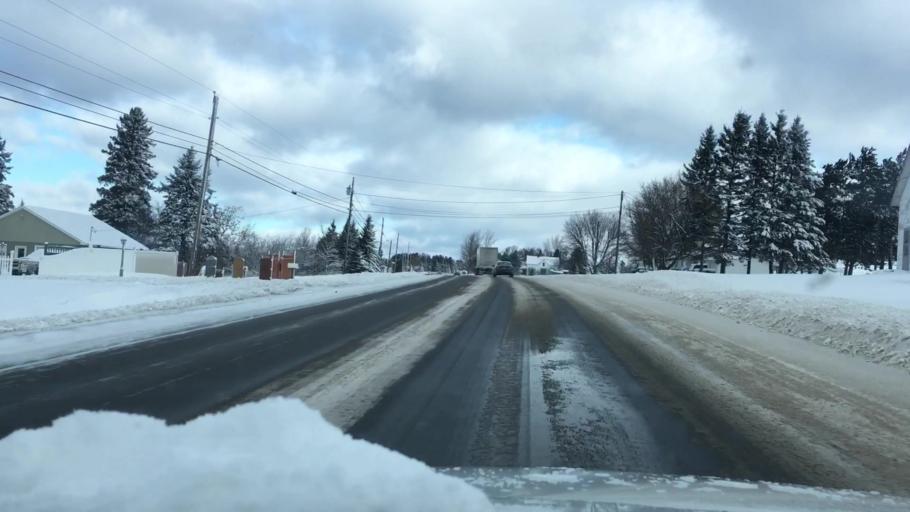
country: US
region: Maine
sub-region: Aroostook County
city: Caribou
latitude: 46.7867
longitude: -67.9894
